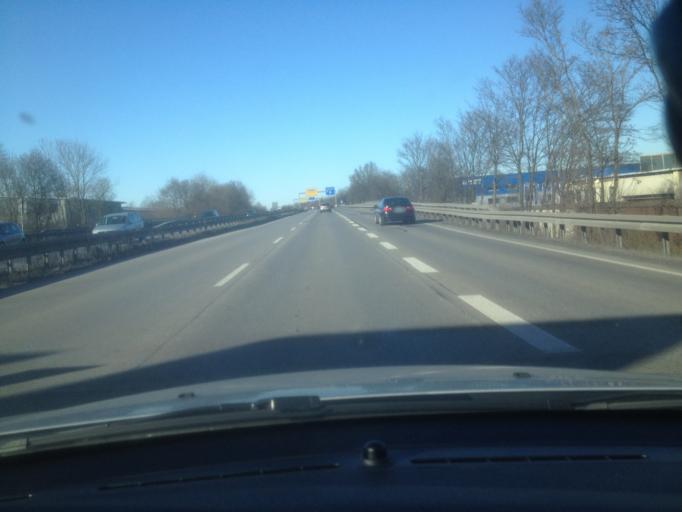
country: DE
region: Bavaria
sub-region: Swabia
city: Gersthofen
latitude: 48.4102
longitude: 10.8737
